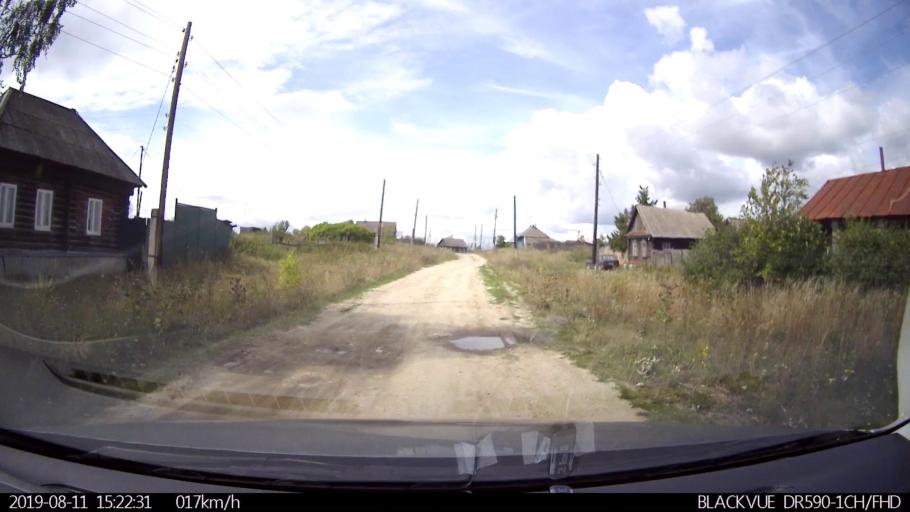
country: RU
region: Ulyanovsk
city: Ignatovka
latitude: 53.8466
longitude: 47.5812
